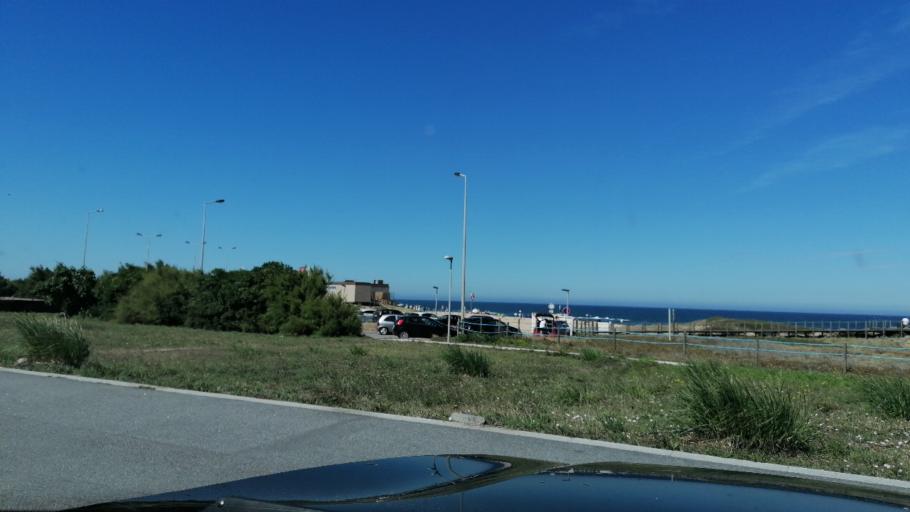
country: PT
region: Porto
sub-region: Matosinhos
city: Lavra
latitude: 41.2497
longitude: -8.7234
